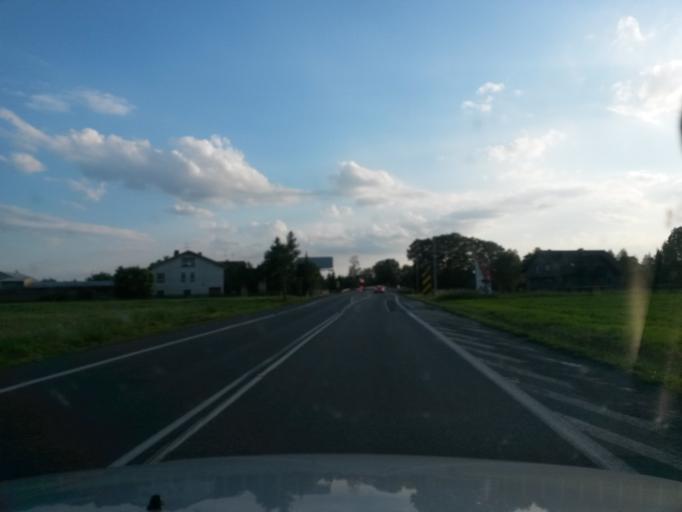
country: PL
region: Lodz Voivodeship
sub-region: Powiat wielunski
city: Wierzchlas
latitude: 51.2411
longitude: 18.6813
